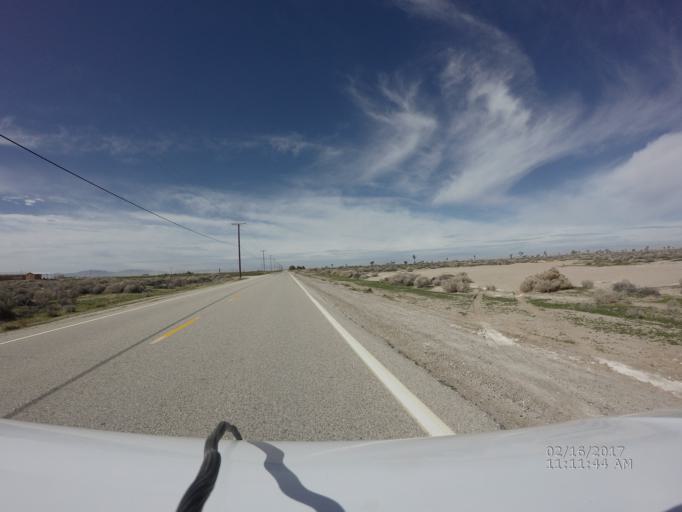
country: US
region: California
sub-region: Los Angeles County
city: Lake Los Angeles
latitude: 34.7195
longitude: -117.9244
